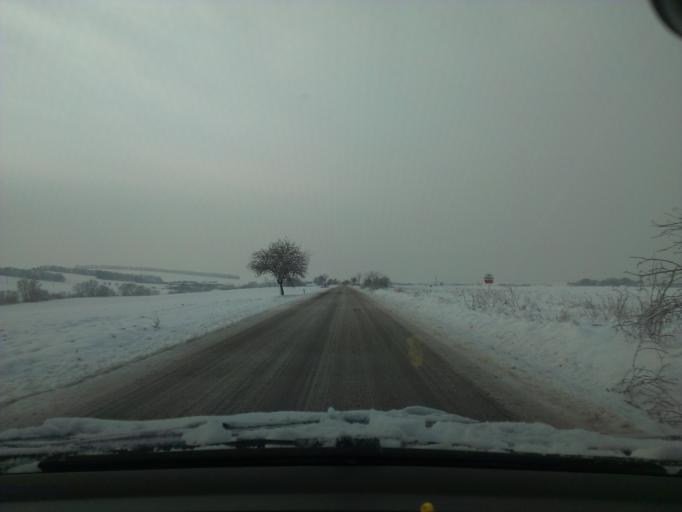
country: SK
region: Trnavsky
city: Hlohovec
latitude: 48.4850
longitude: 17.9891
